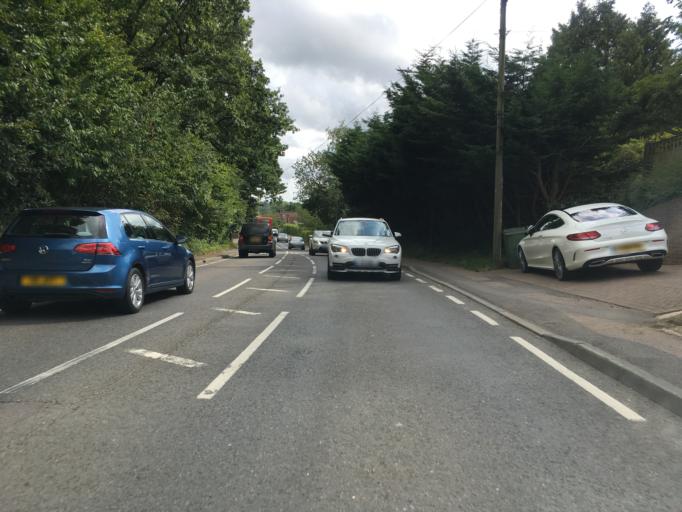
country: GB
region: England
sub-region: Kent
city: Tenterden
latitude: 51.0873
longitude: 0.6902
